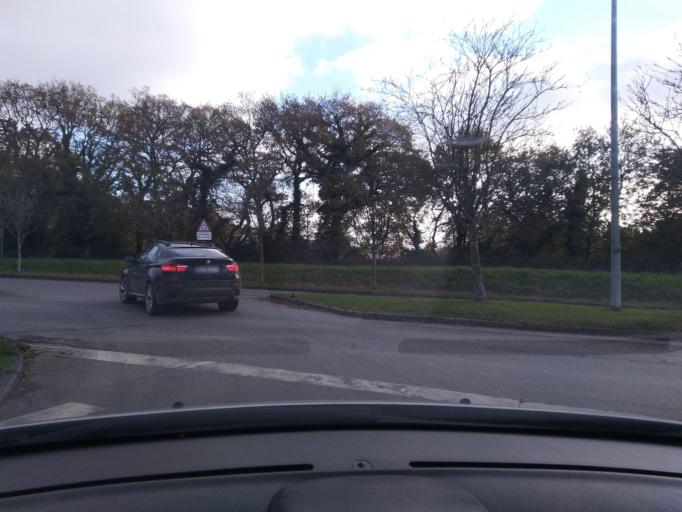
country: FR
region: Brittany
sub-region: Departement du Finistere
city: Morlaix
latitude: 48.5881
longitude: -3.8152
